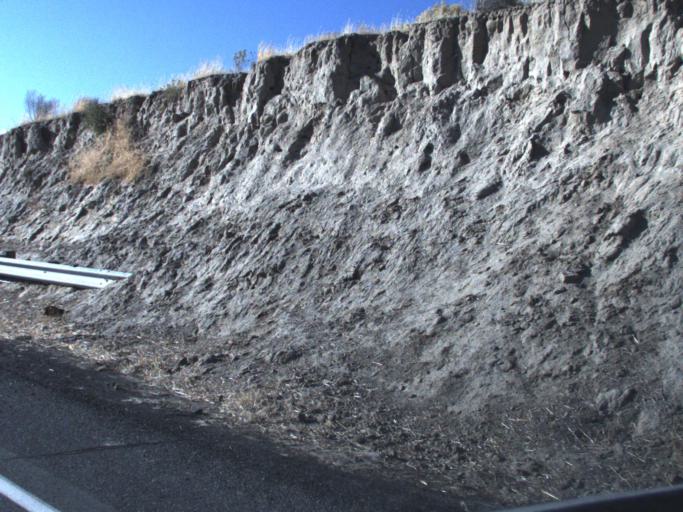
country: US
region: Washington
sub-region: Walla Walla County
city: Garrett
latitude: 46.2969
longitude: -118.6582
